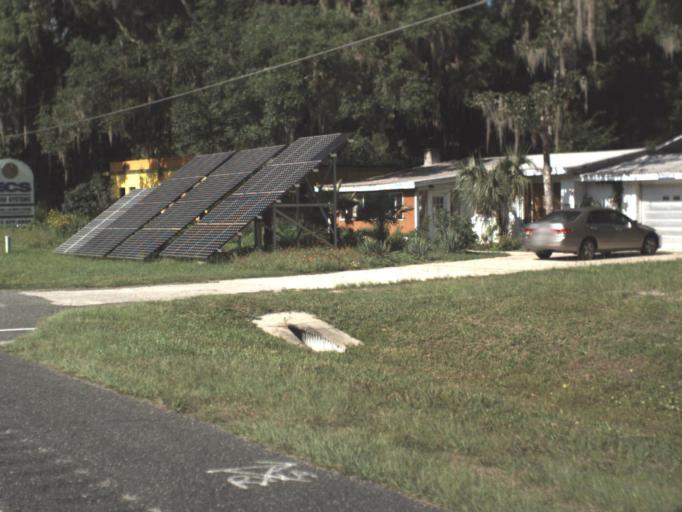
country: US
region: Florida
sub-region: Alachua County
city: Gainesville
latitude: 29.5965
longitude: -82.3392
